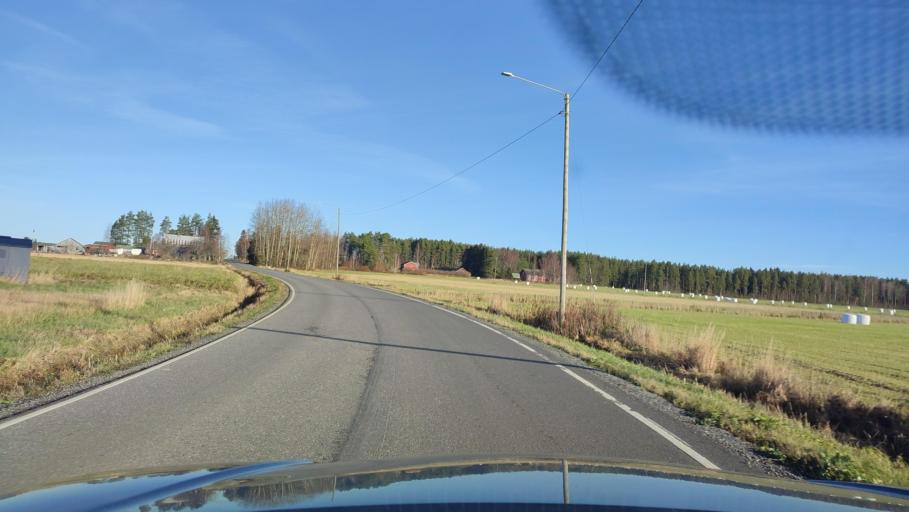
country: FI
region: Southern Ostrobothnia
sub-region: Suupohja
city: Karijoki
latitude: 62.2855
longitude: 21.7159
